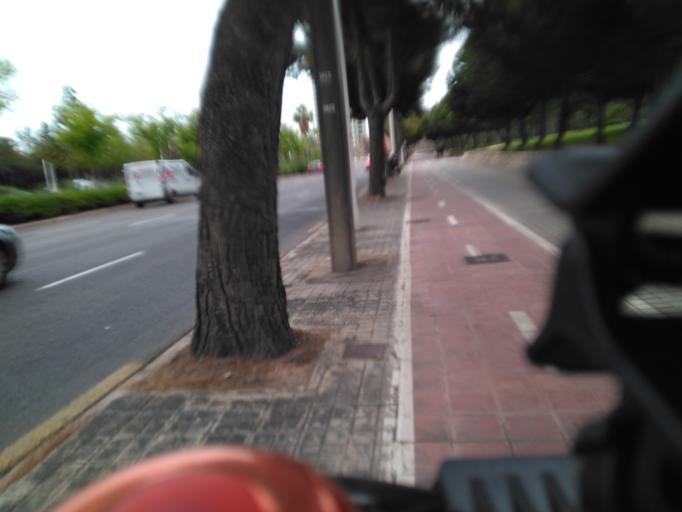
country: ES
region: Valencia
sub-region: Provincia de Valencia
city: Mislata
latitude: 39.4759
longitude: -0.4065
